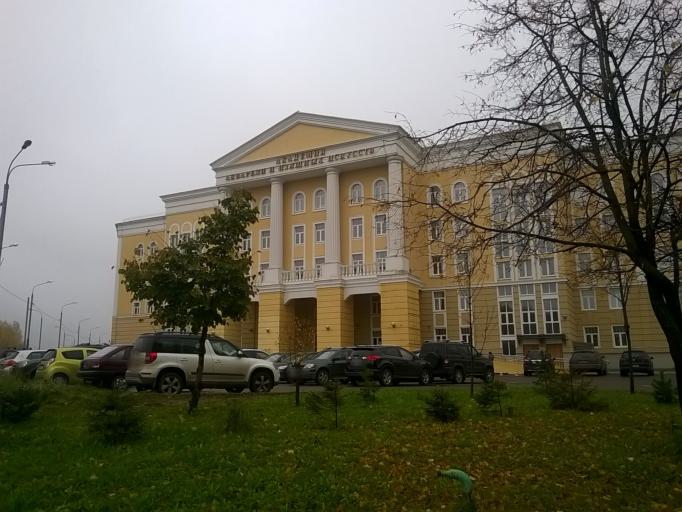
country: RU
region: Moscow
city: Tyoply Stan
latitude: 55.6344
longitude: 37.4801
